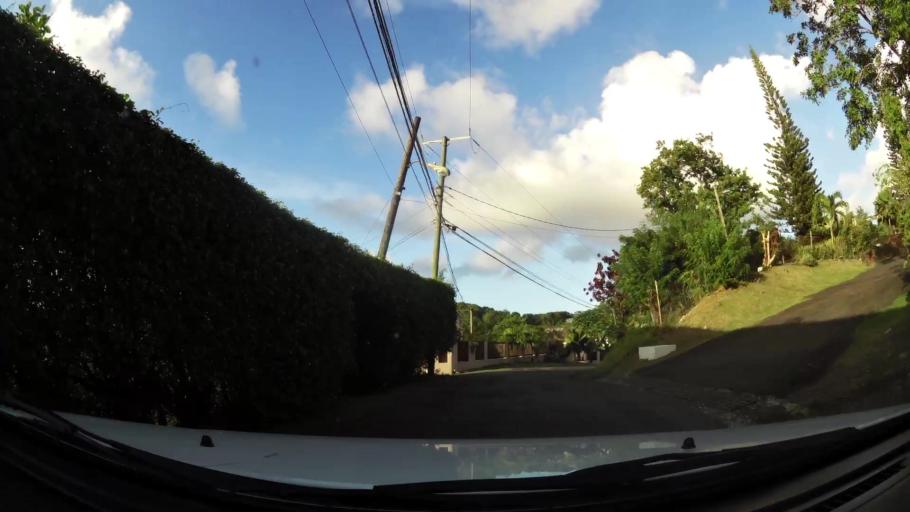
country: LC
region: Gros-Islet
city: Gros Islet
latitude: 14.0650
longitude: -60.9427
